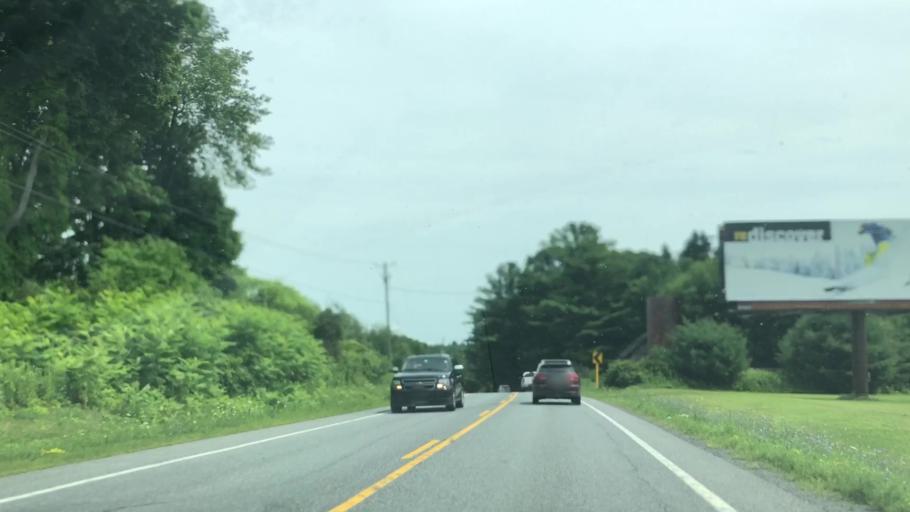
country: US
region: New York
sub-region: Warren County
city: Queensbury
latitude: 43.4044
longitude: -73.5429
